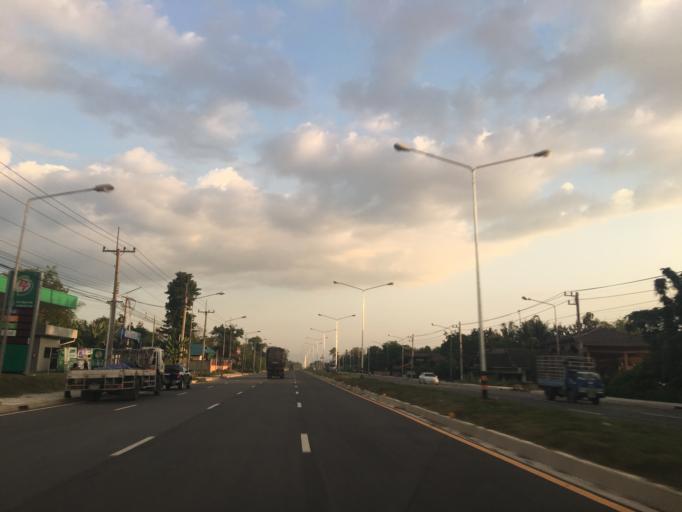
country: TH
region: Phrae
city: Song
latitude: 18.3947
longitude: 100.1908
